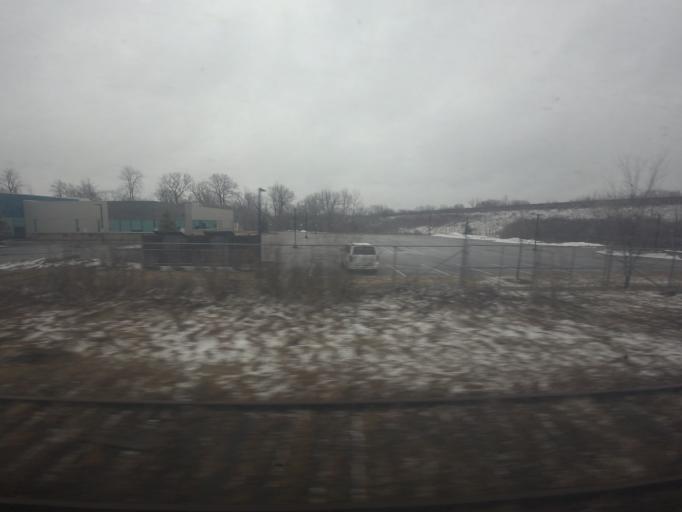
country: CA
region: Ontario
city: Brockville
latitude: 44.6065
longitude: -75.6934
